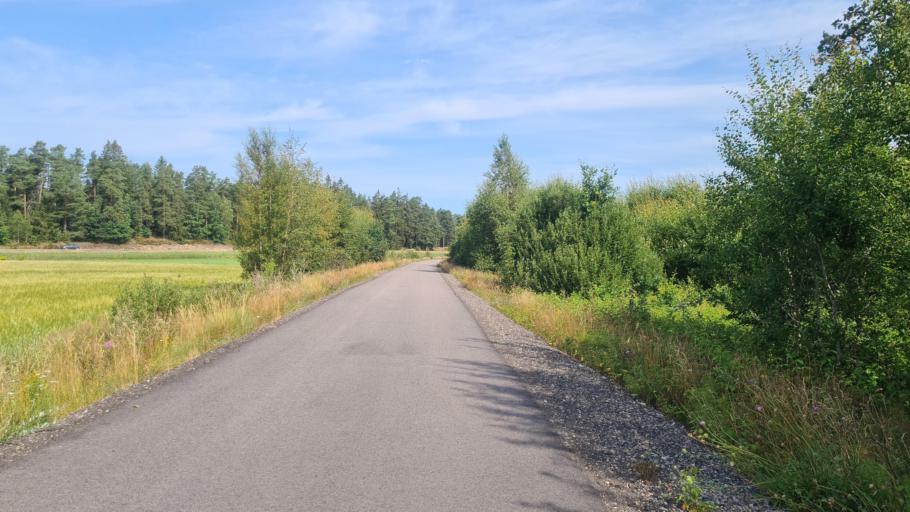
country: SE
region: Kronoberg
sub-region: Ljungby Kommun
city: Ljungby
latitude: 56.8649
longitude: 13.9773
